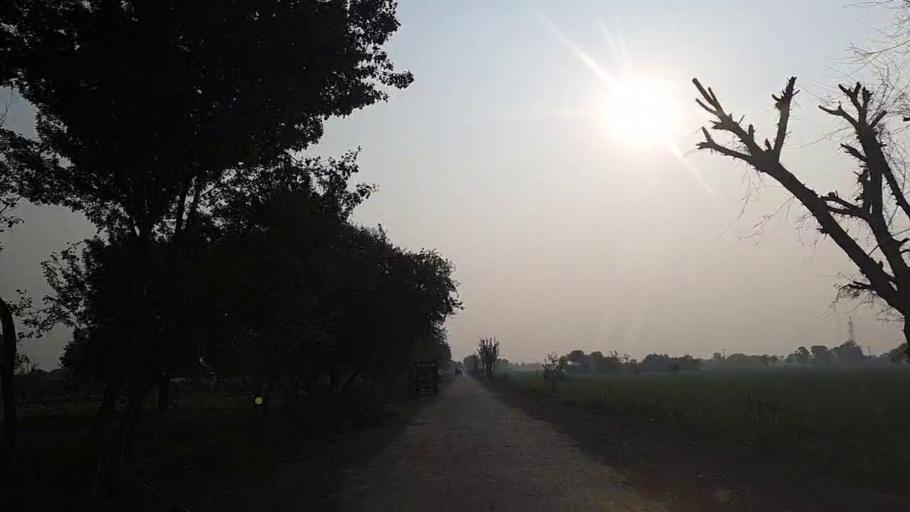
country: PK
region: Sindh
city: Nawabshah
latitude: 26.2287
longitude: 68.4832
